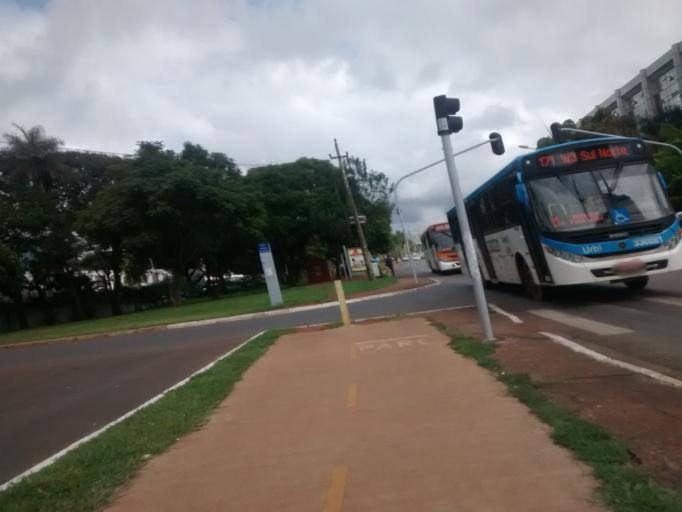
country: BR
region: Federal District
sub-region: Brasilia
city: Brasilia
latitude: -15.7833
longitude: -47.8874
